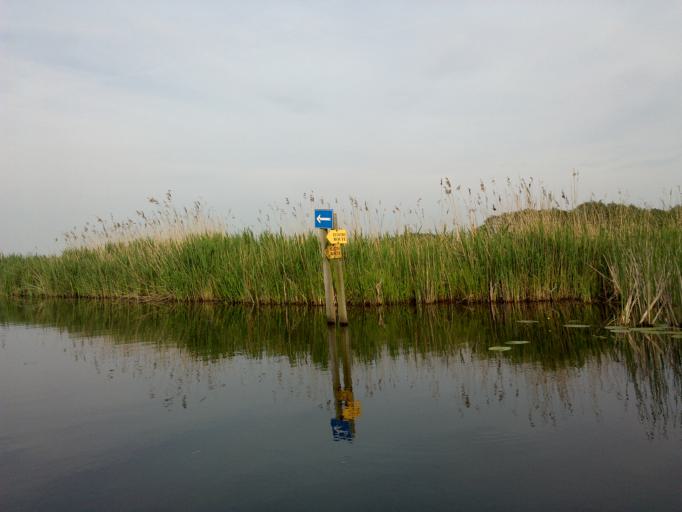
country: NL
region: South Holland
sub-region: Gemeente Nieuwkoop
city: Nieuwkoop
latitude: 52.1402
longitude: 4.7987
